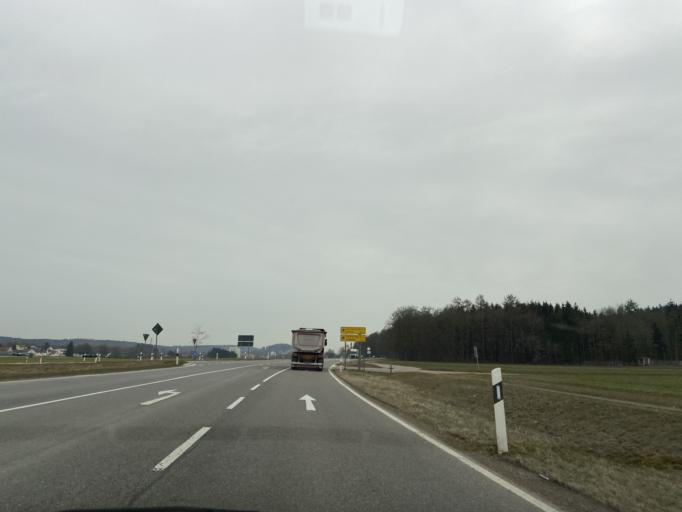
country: DE
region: Baden-Wuerttemberg
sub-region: Tuebingen Region
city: Ostrach
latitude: 47.9661
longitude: 9.3619
